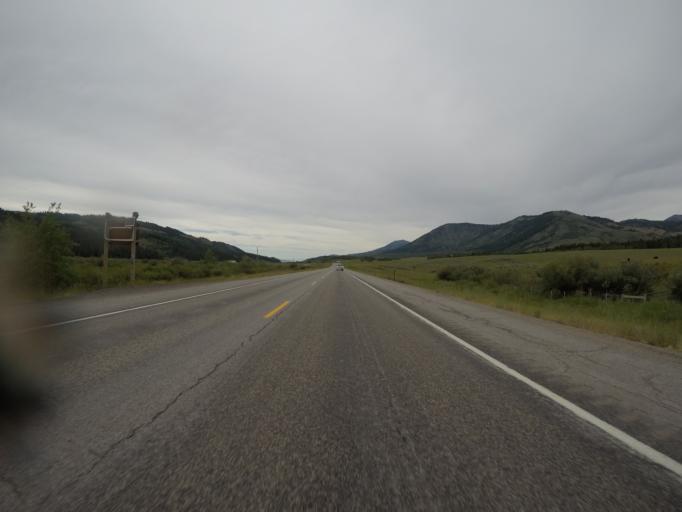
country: US
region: Wyoming
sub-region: Lincoln County
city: Afton
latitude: 42.5519
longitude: -110.8942
